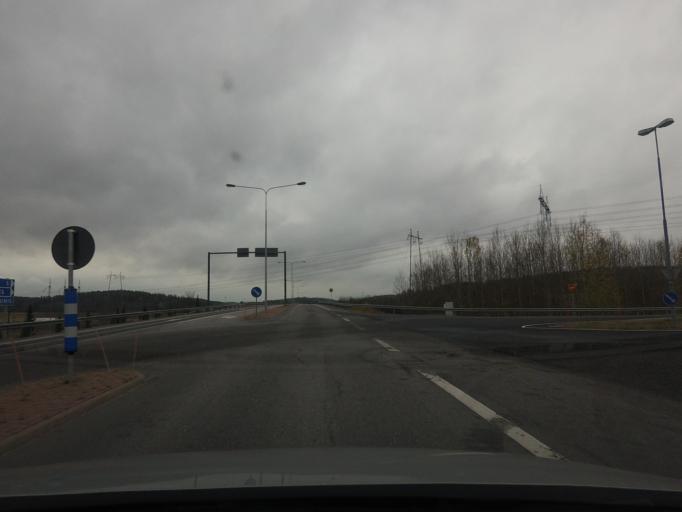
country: FI
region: Varsinais-Suomi
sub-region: Turku
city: Paimio
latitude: 60.4439
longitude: 22.6034
